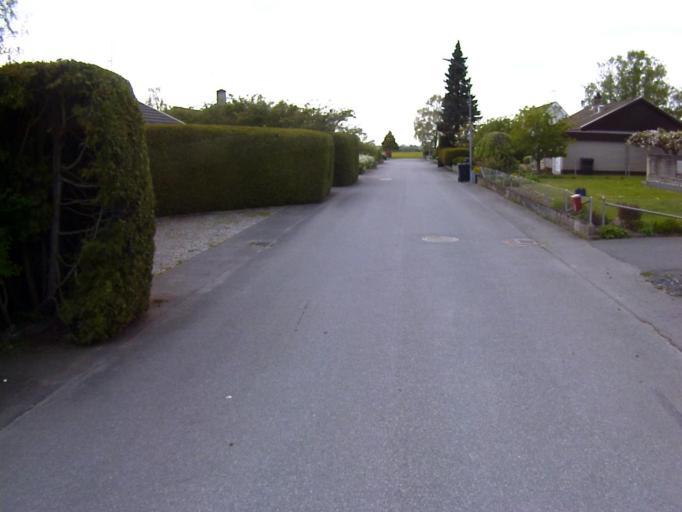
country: SE
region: Skane
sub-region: Kristianstads Kommun
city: Fjalkinge
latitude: 56.0484
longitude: 14.2814
